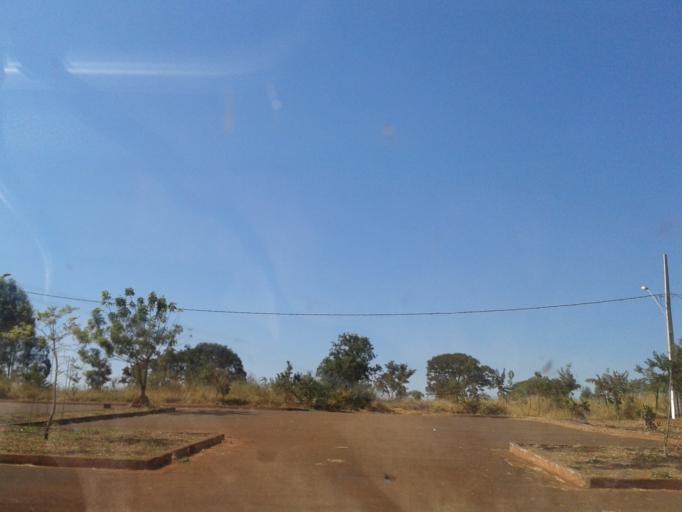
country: BR
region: Minas Gerais
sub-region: Ituiutaba
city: Ituiutaba
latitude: -19.0046
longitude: -49.4760
